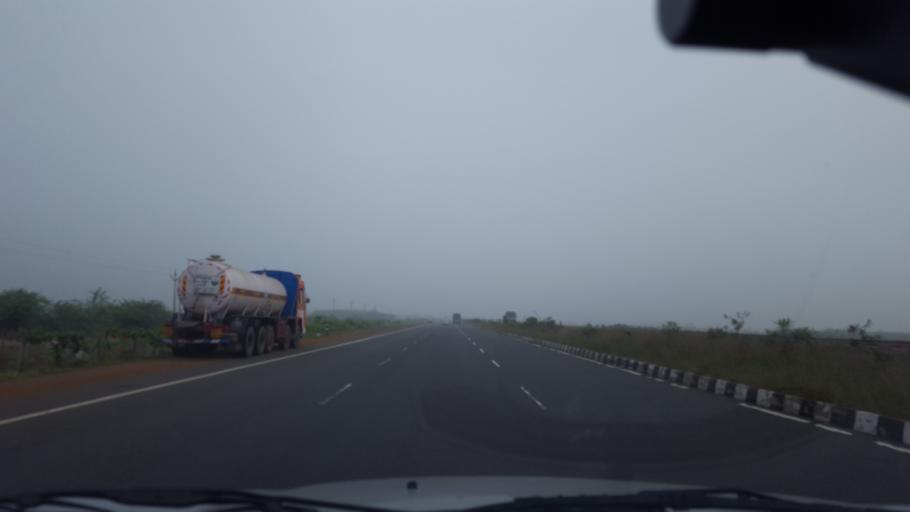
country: IN
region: Andhra Pradesh
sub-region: Prakasam
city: Ongole
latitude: 15.4842
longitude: 80.0625
